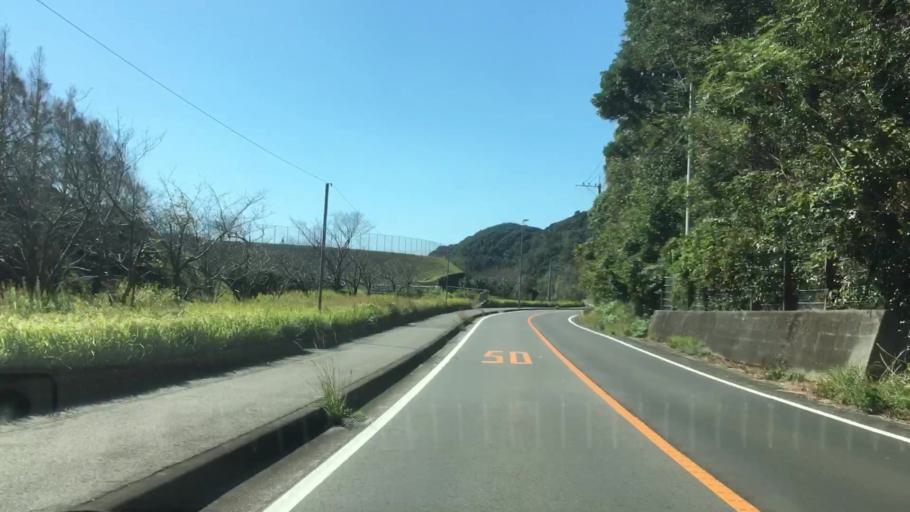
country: JP
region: Nagasaki
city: Sasebo
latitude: 33.0322
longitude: 129.6053
